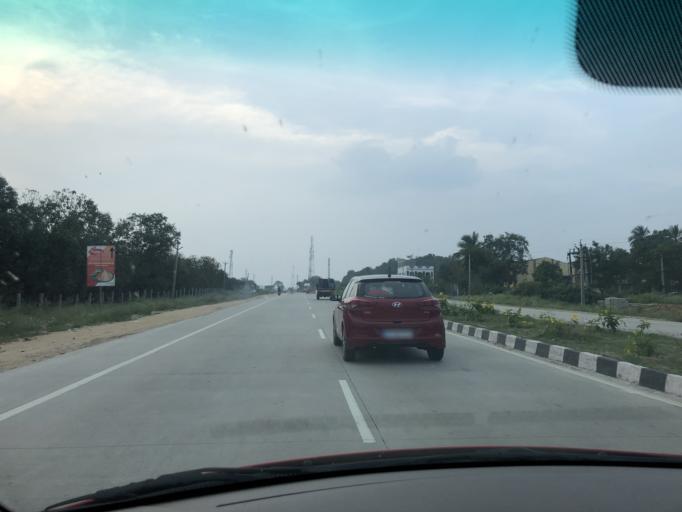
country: IN
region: Andhra Pradesh
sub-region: Chittoor
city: Chittoor
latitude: 13.1956
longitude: 79.0090
